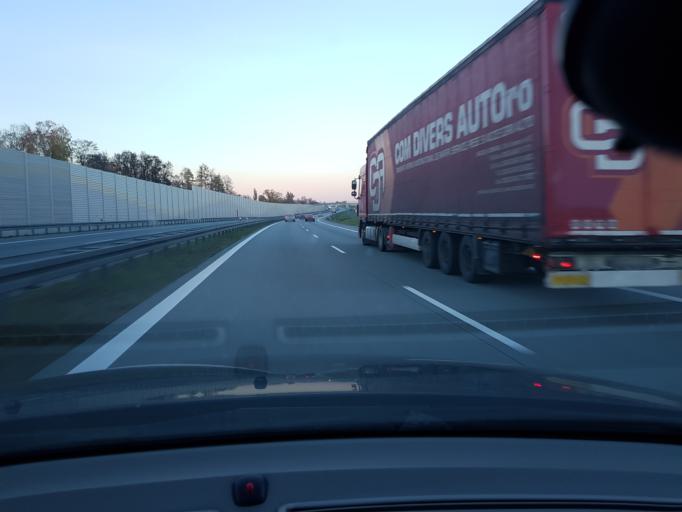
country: PL
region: Lodz Voivodeship
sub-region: Powiat rawski
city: Rawa Mazowiecka
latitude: 51.7834
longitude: 20.2786
